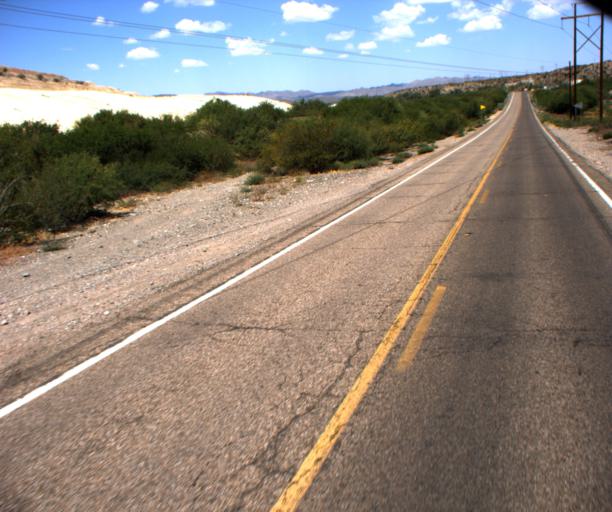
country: US
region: Arizona
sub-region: Pinal County
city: Kearny
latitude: 33.0092
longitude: -110.8049
